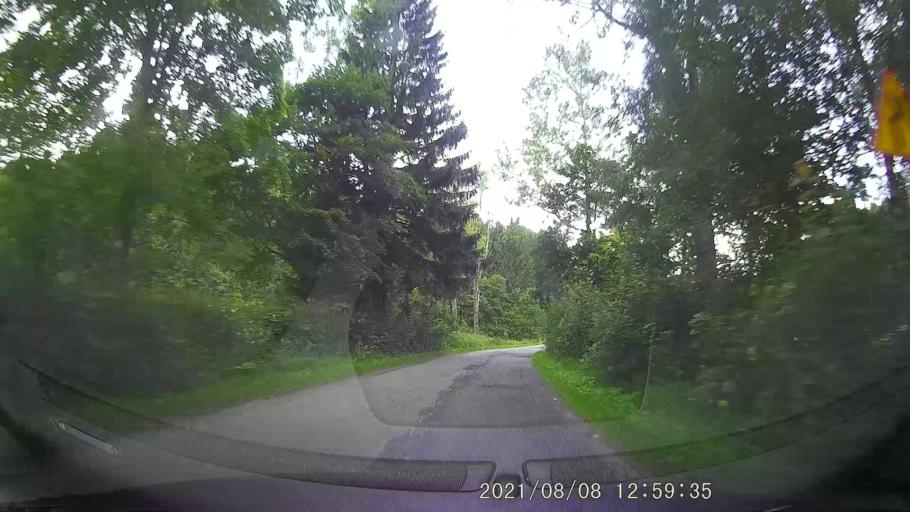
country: PL
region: Lower Silesian Voivodeship
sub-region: Powiat klodzki
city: Duszniki-Zdroj
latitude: 50.4107
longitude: 16.3477
